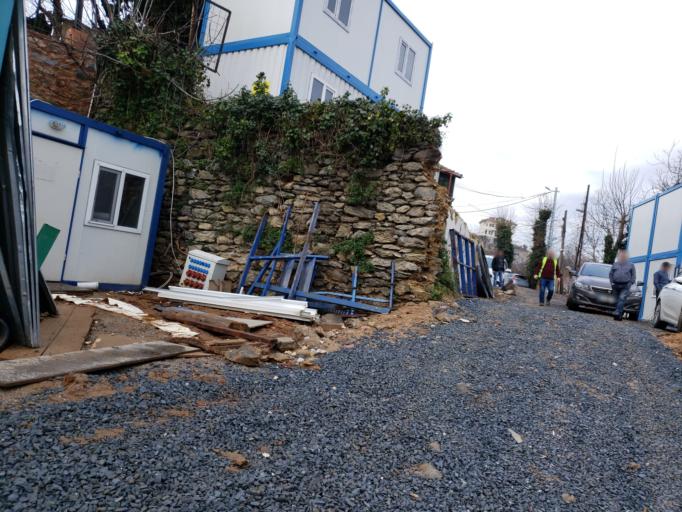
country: TR
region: Istanbul
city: Arikoey
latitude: 41.1684
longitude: 29.0531
